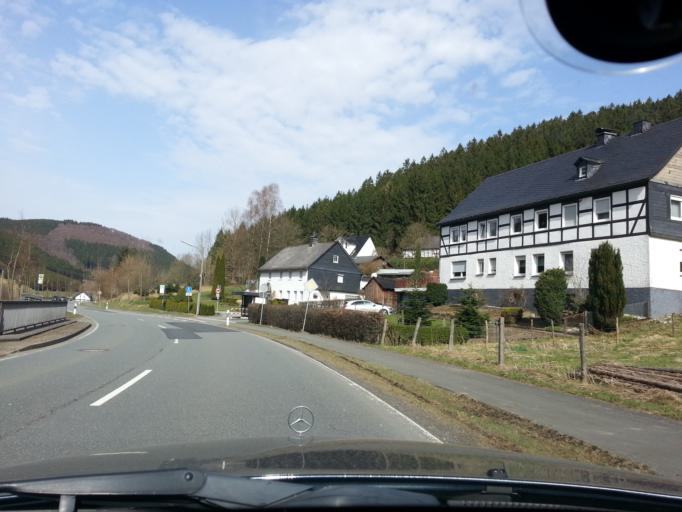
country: DE
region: North Rhine-Westphalia
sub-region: Regierungsbezirk Arnsberg
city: Meschede
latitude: 51.2810
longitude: 8.3383
